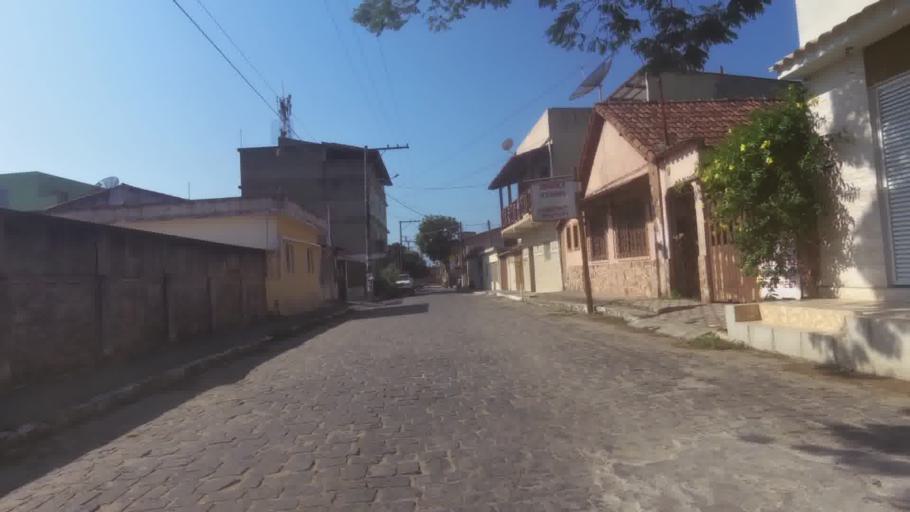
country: BR
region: Espirito Santo
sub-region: Itapemirim
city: Itapemirim
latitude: -21.0100
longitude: -40.8125
